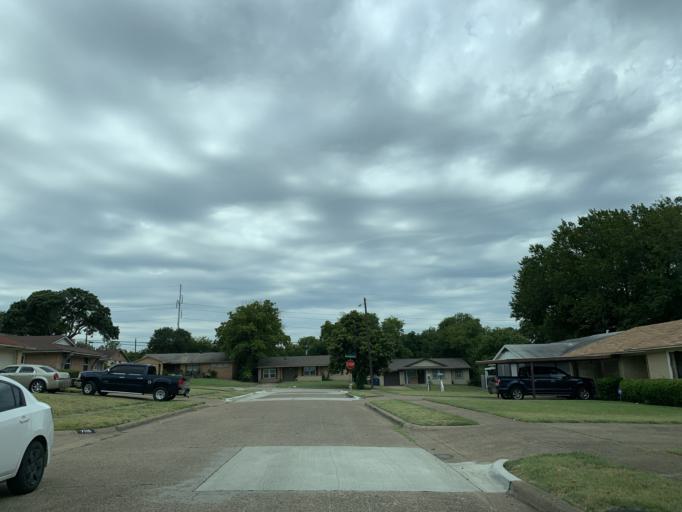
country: US
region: Texas
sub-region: Dallas County
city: DeSoto
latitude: 32.6611
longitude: -96.8288
